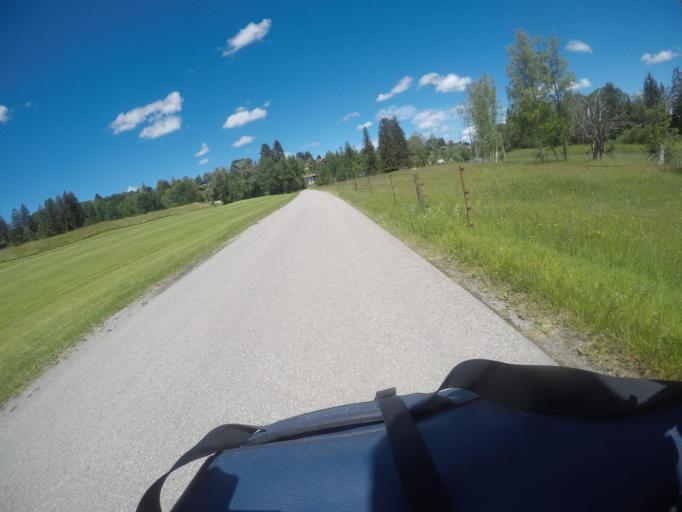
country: DE
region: Bavaria
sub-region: Upper Bavaria
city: Prem
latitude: 47.6891
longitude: 10.7969
